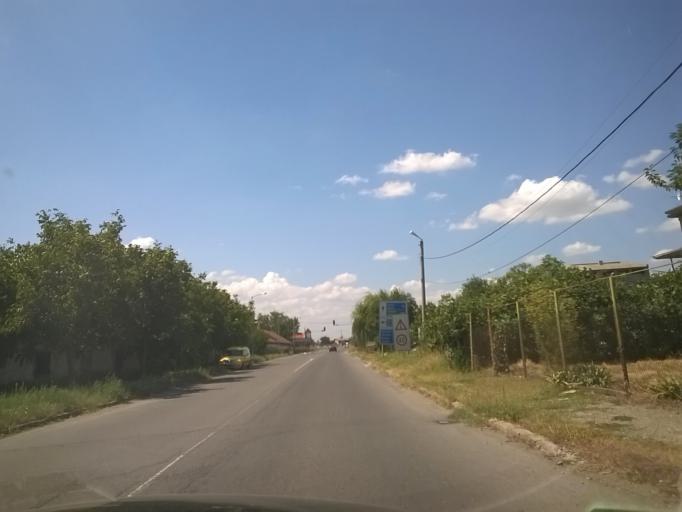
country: BG
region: Burgas
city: Aheloy
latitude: 42.6551
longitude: 27.5697
